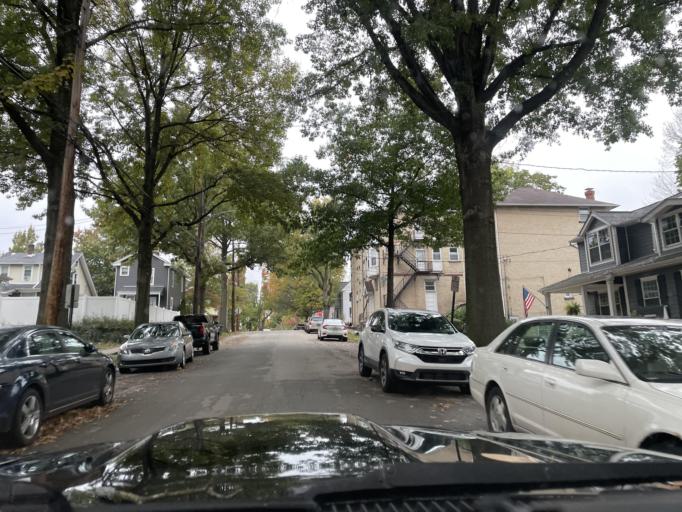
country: US
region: Pennsylvania
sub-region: Allegheny County
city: Oakmont
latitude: 40.5166
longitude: -79.8395
